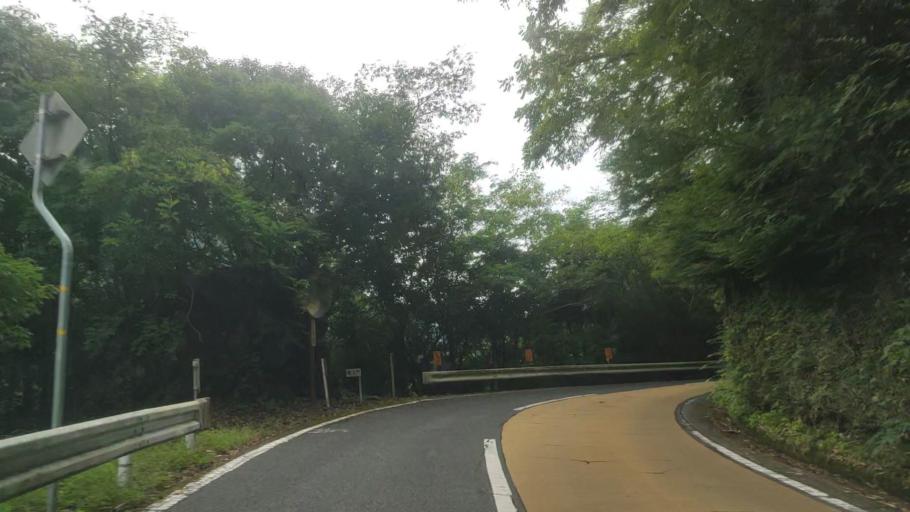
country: JP
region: Wakayama
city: Koya
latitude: 34.2441
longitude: 135.5480
